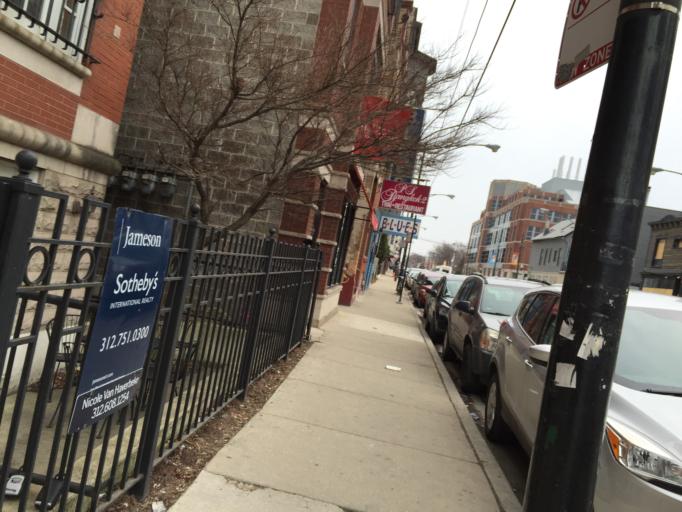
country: US
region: Illinois
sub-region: Cook County
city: Chicago
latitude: 41.9282
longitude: -87.6488
